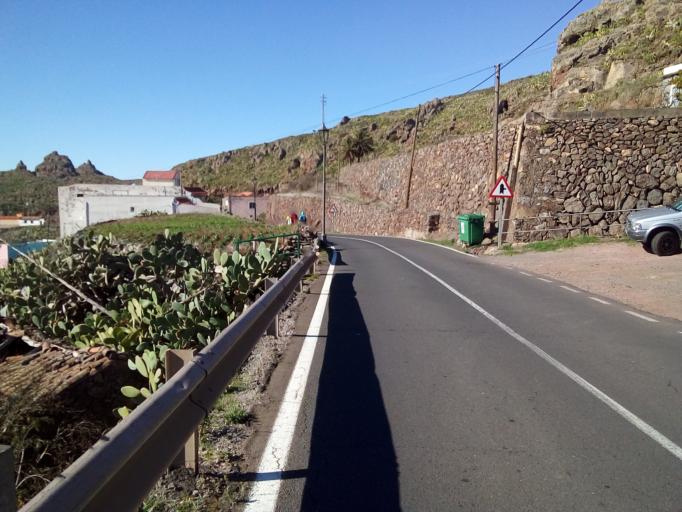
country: ES
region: Canary Islands
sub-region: Provincia de Santa Cruz de Tenerife
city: Vallehermosa
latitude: 28.1326
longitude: -17.3209
